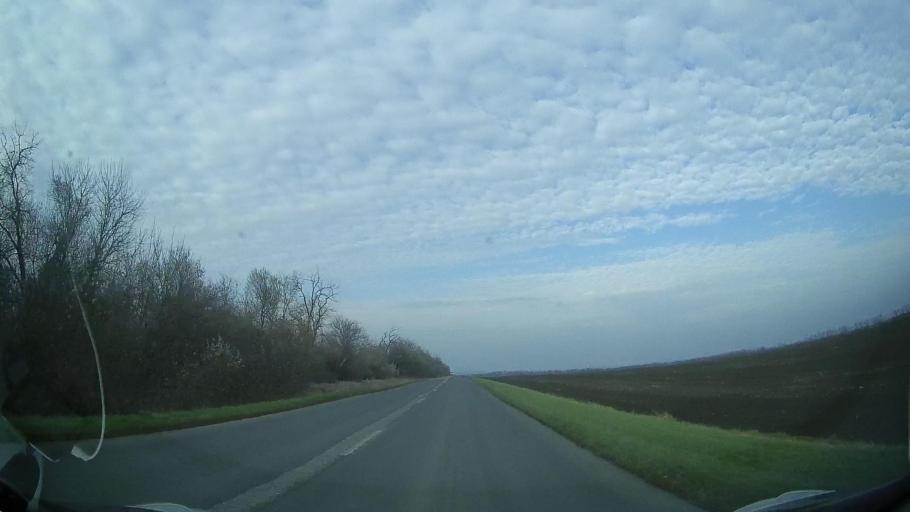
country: RU
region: Rostov
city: Bagayevskaya
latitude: 47.0808
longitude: 40.3915
